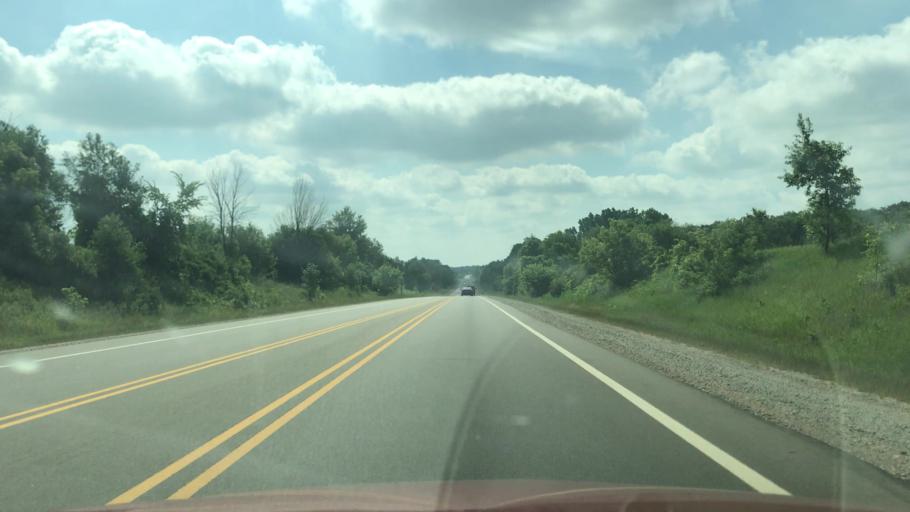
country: US
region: Michigan
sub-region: Kent County
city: Kent City
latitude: 43.2112
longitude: -85.7495
